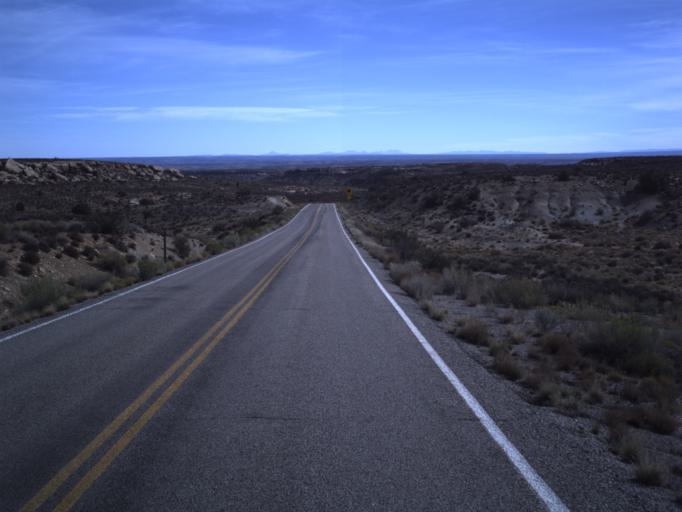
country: US
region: Utah
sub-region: San Juan County
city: Blanding
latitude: 37.3265
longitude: -109.3278
